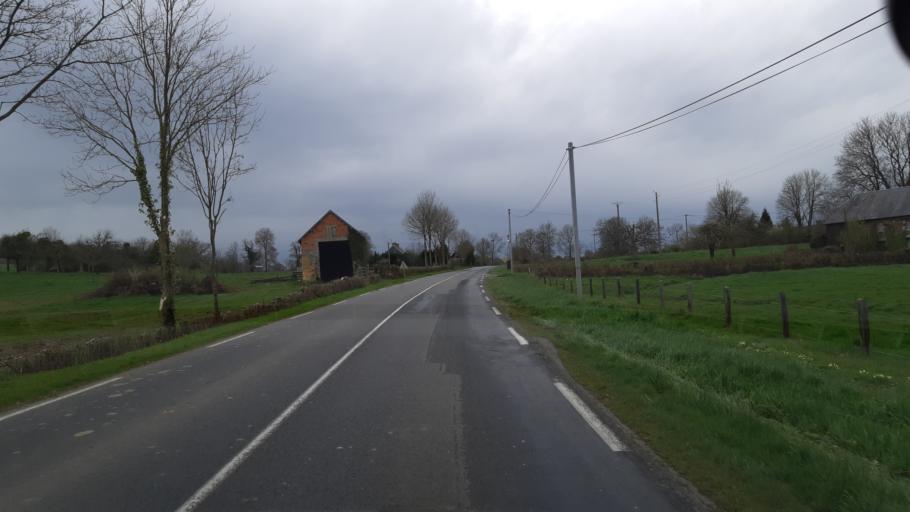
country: FR
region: Lower Normandy
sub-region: Departement de la Manche
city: Percy
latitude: 48.9566
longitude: -1.2013
